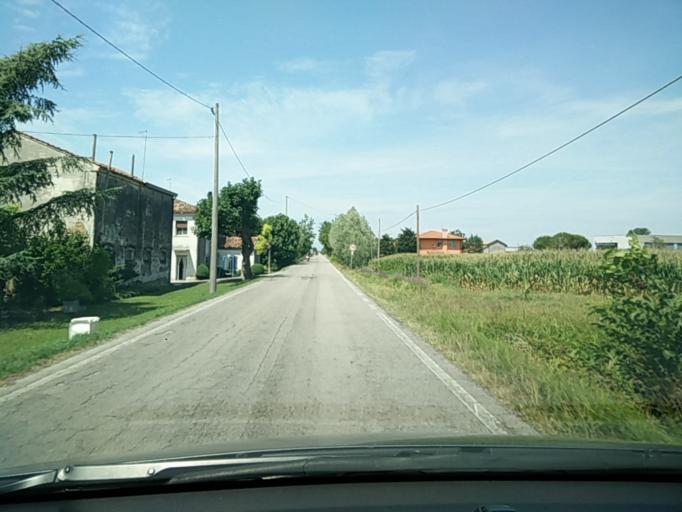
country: IT
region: Veneto
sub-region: Provincia di Venezia
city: Passarella
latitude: 45.6024
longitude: 12.5894
